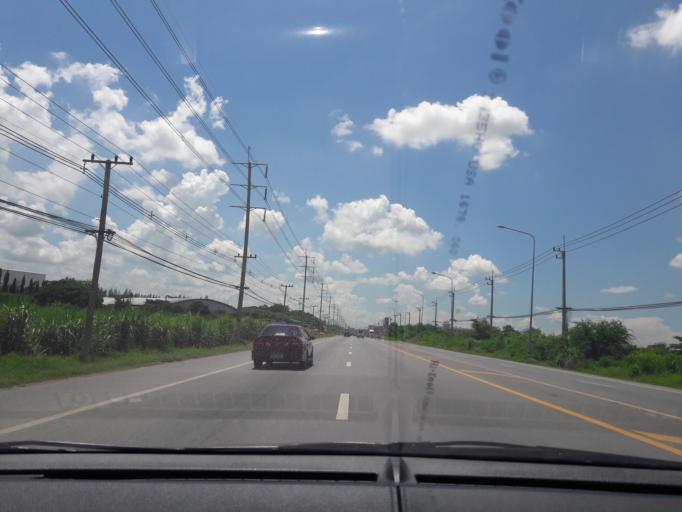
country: TH
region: Nakhon Pathom
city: Kamphaeng Saen
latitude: 14.0146
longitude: 100.0153
